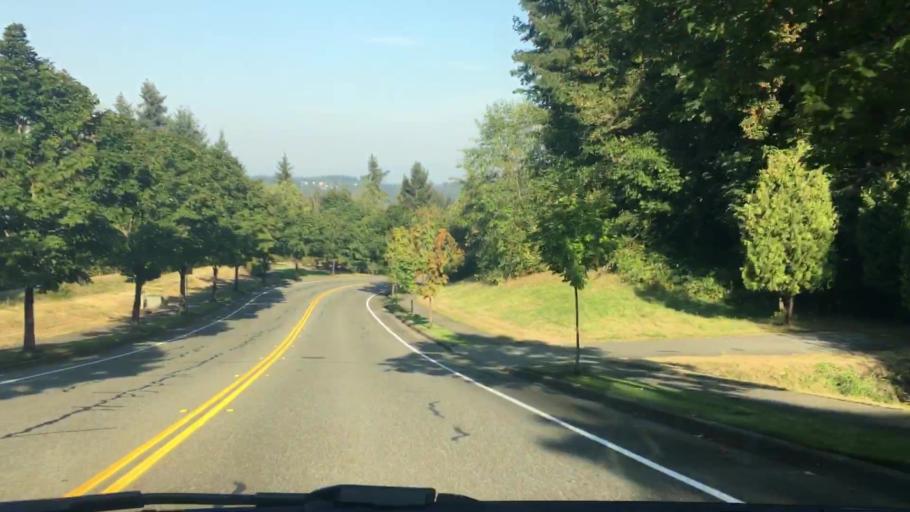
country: US
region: Washington
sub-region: King County
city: West Lake Sammamish
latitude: 47.5583
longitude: -122.0944
